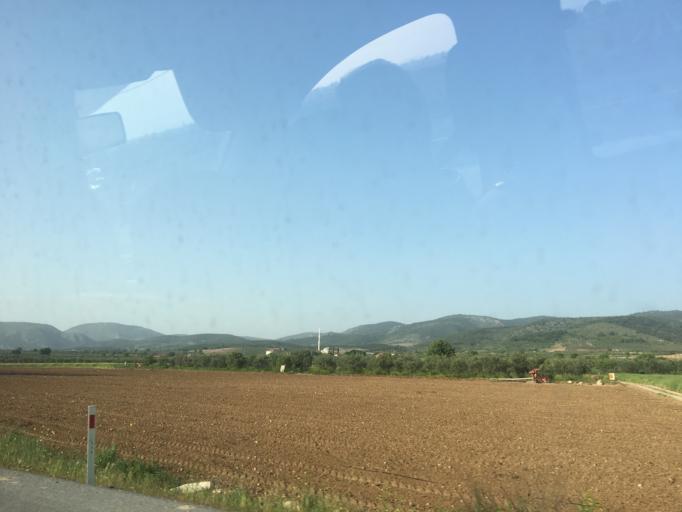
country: TR
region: Manisa
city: Golmarmara
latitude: 38.7885
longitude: 27.9027
